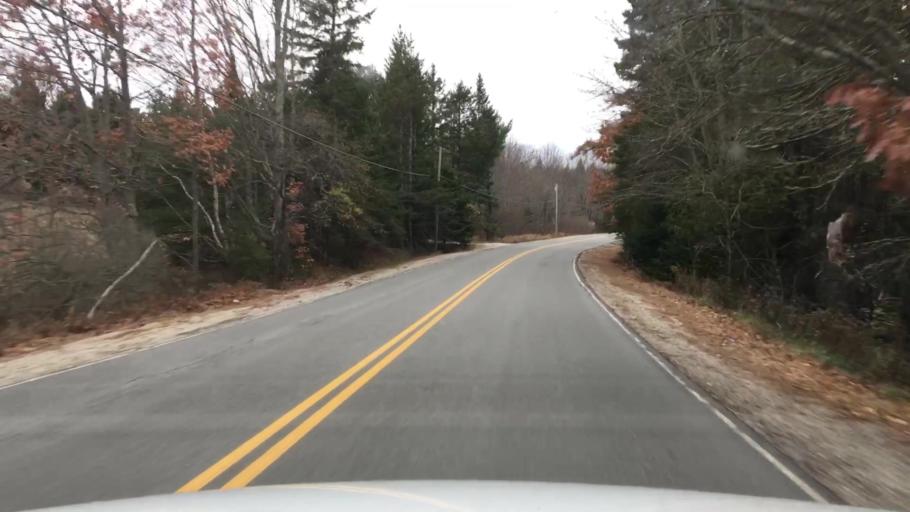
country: US
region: Maine
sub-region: Hancock County
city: Penobscot
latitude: 44.4318
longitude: -68.6291
